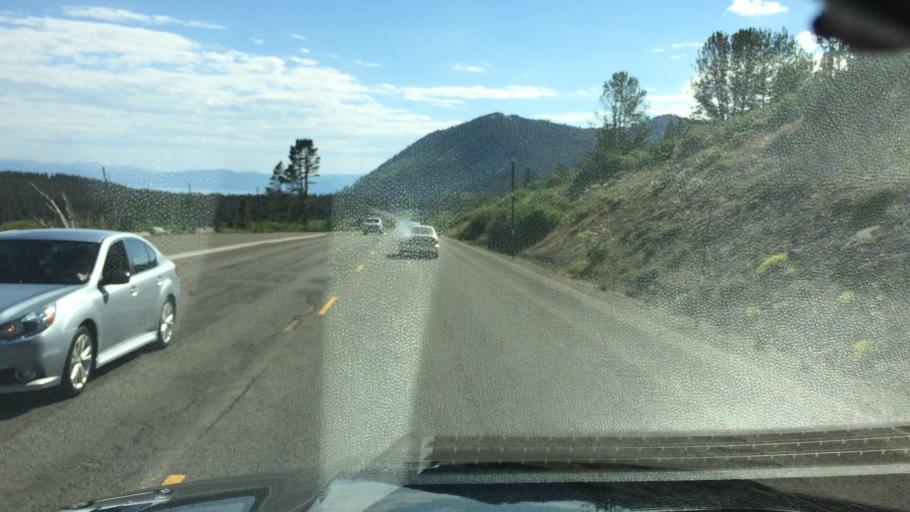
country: US
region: Nevada
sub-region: Washoe County
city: Incline Village
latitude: 39.3084
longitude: -119.9074
